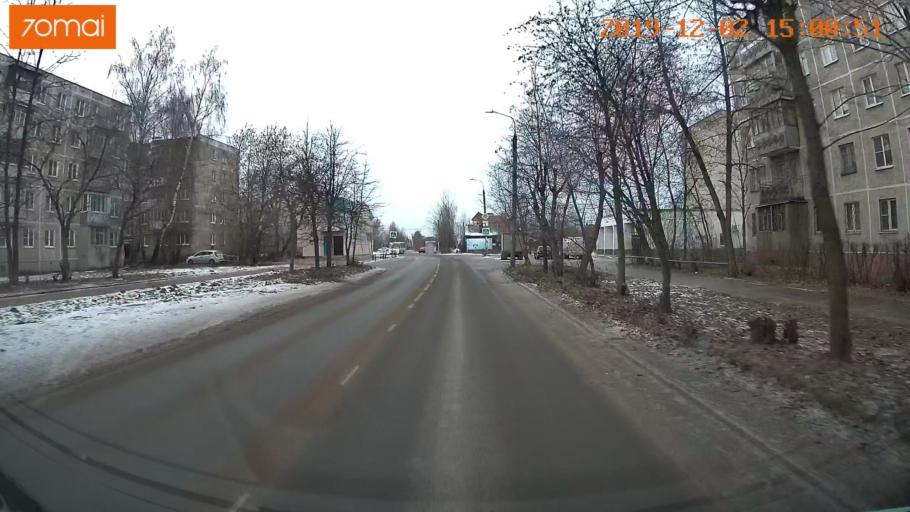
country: RU
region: Ivanovo
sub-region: Gorod Ivanovo
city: Ivanovo
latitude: 56.9726
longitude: 41.0015
